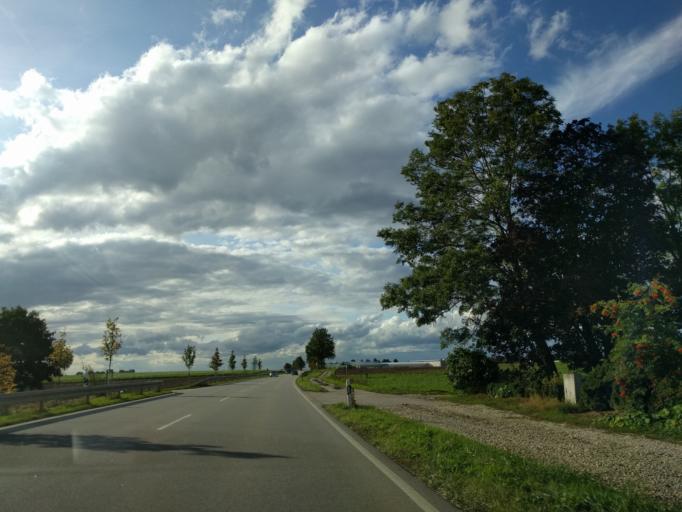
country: DE
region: Bavaria
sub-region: Lower Bavaria
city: Stephansposching
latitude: 48.7987
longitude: 12.8106
